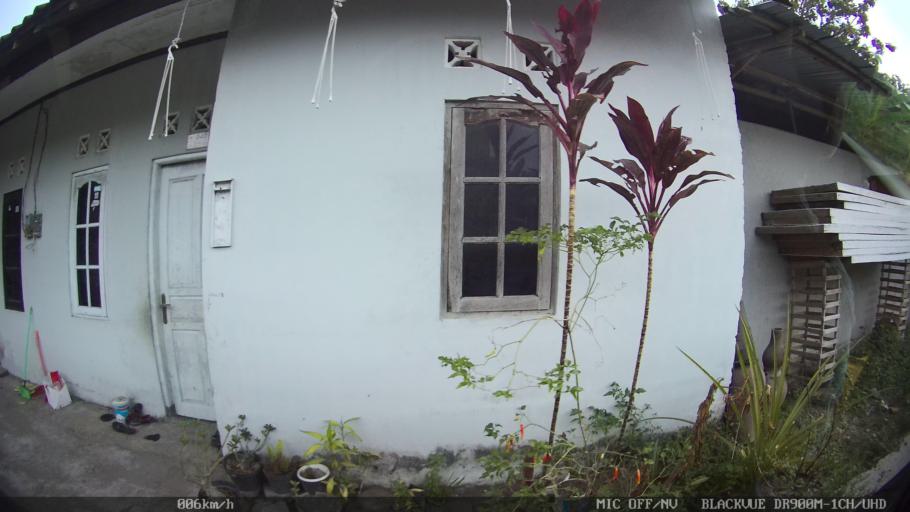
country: ID
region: Daerah Istimewa Yogyakarta
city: Yogyakarta
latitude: -7.8144
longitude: 110.4056
